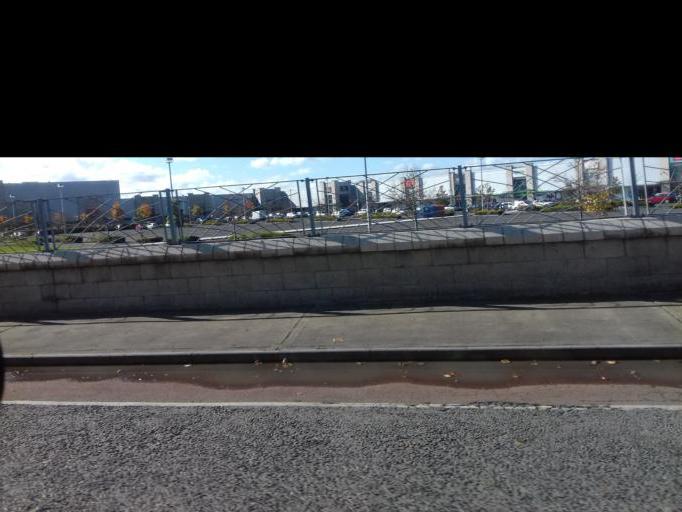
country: IE
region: Leinster
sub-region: An Mhi
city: Ashbourne
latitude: 53.5231
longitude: -6.4132
